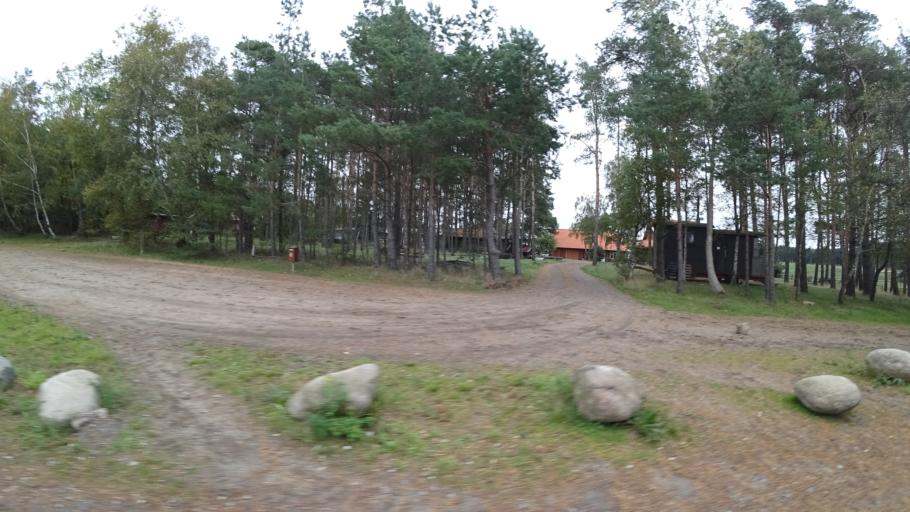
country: SE
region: Skane
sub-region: Kavlinge Kommun
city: Hofterup
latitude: 55.8229
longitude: 12.9513
